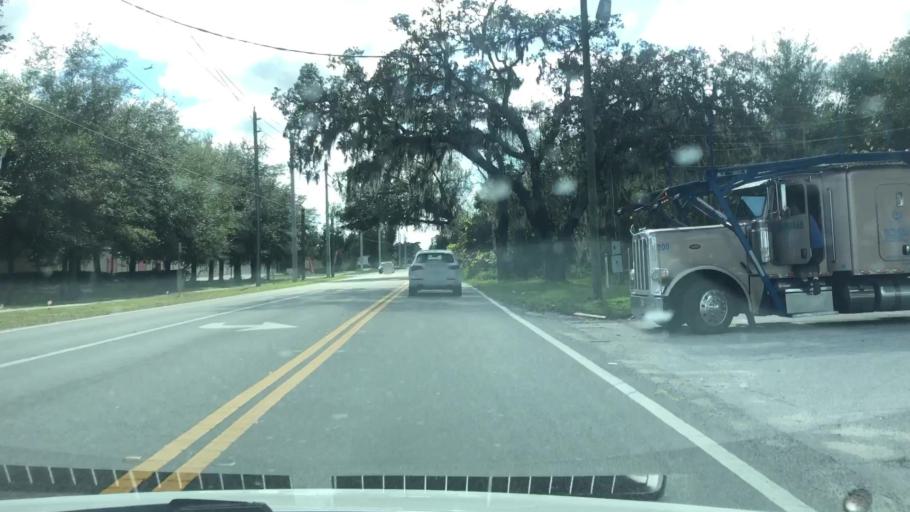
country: US
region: Florida
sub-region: Seminole County
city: Heathrow
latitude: 28.8115
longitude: -81.3631
